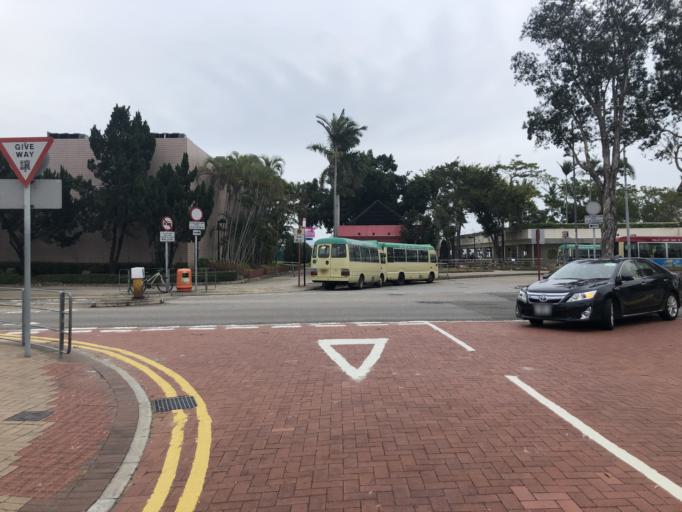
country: HK
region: Sai Kung
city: Sai Kung
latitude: 22.3834
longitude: 114.2745
